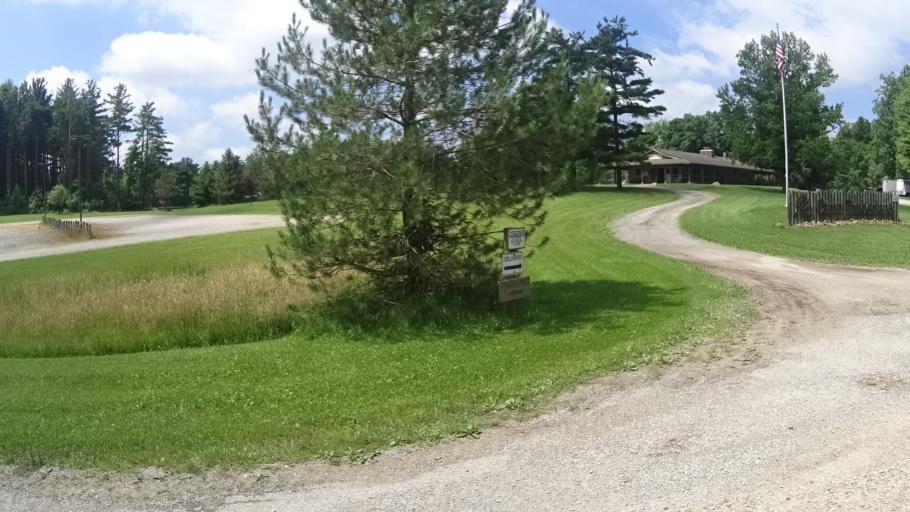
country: US
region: Ohio
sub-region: Lorain County
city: Camden
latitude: 41.2965
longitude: -82.3432
